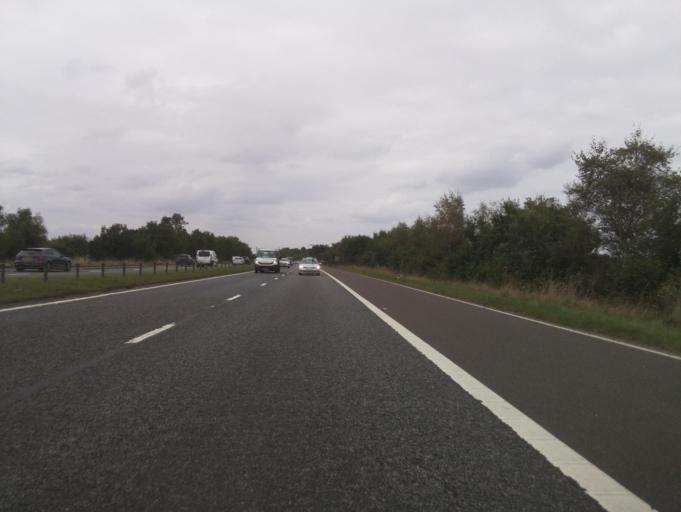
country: GB
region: England
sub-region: County Durham
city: West Rainton
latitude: 54.8031
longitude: -1.5233
